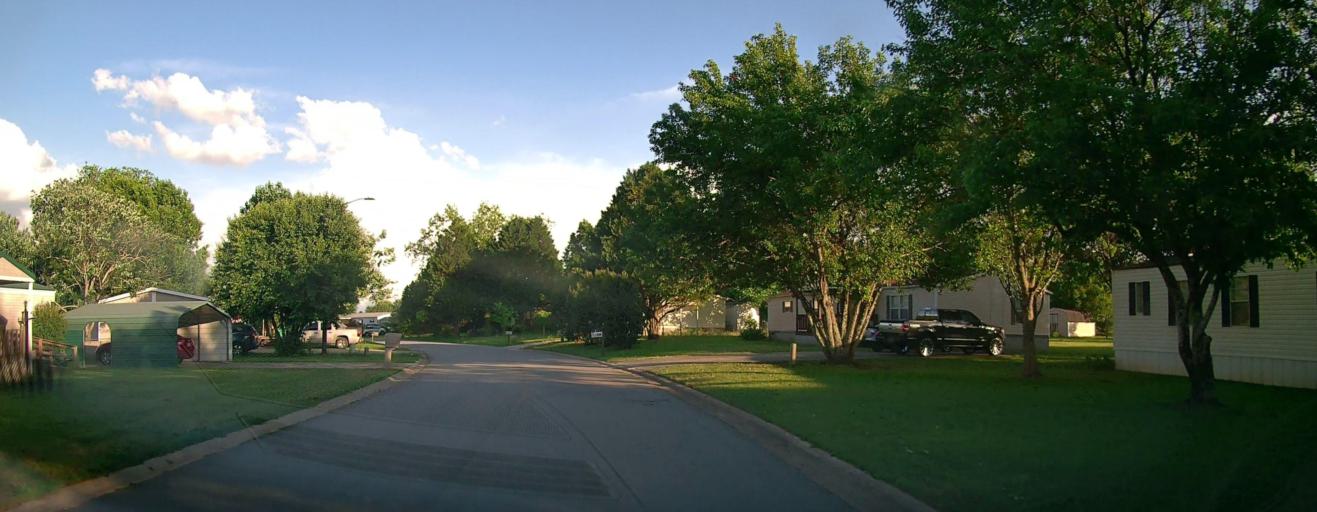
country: US
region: Georgia
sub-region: Houston County
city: Centerville
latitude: 32.6373
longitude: -83.7242
